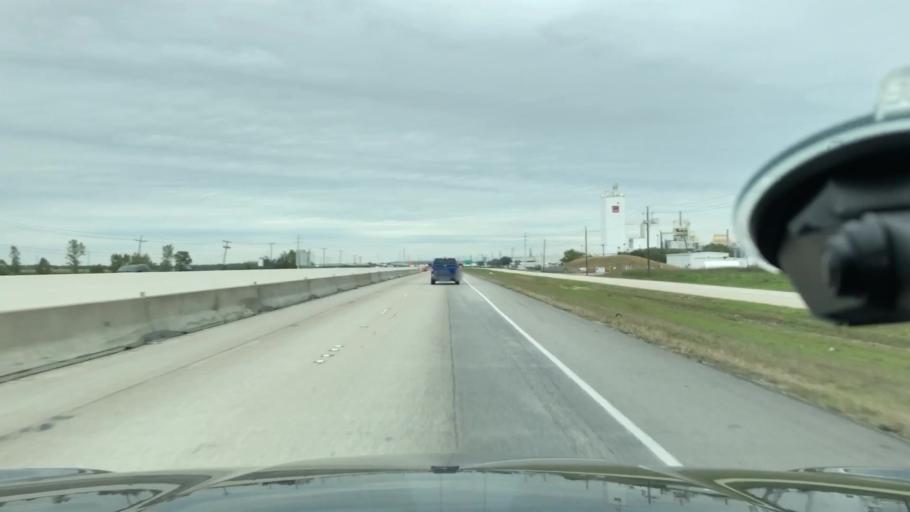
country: US
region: Texas
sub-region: Ellis County
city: Waxahachie
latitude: 32.4361
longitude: -96.8548
